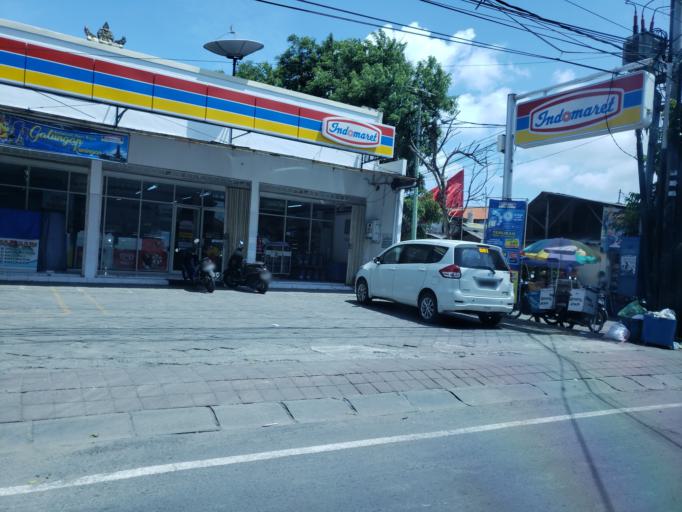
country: ID
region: Bali
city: Kelanabian
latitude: -8.7536
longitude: 115.1778
